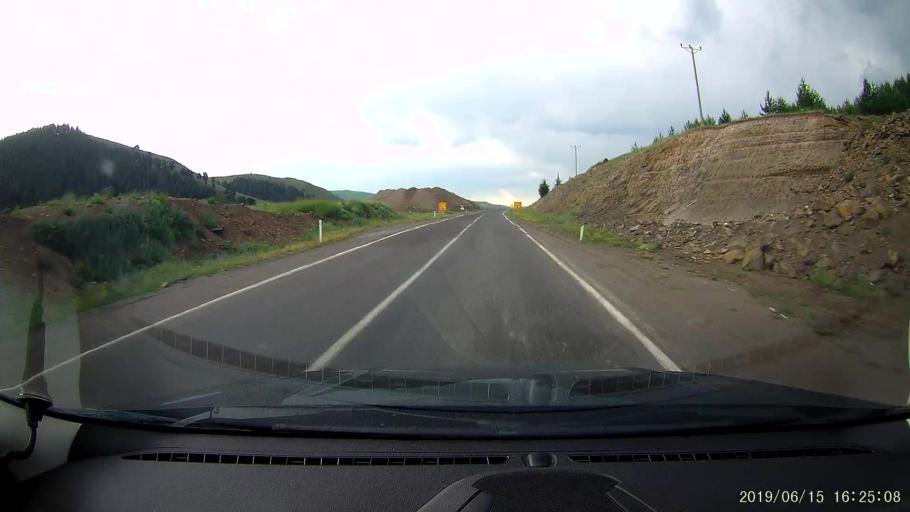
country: TR
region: Ardahan
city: Hanak
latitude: 41.1576
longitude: 42.8715
